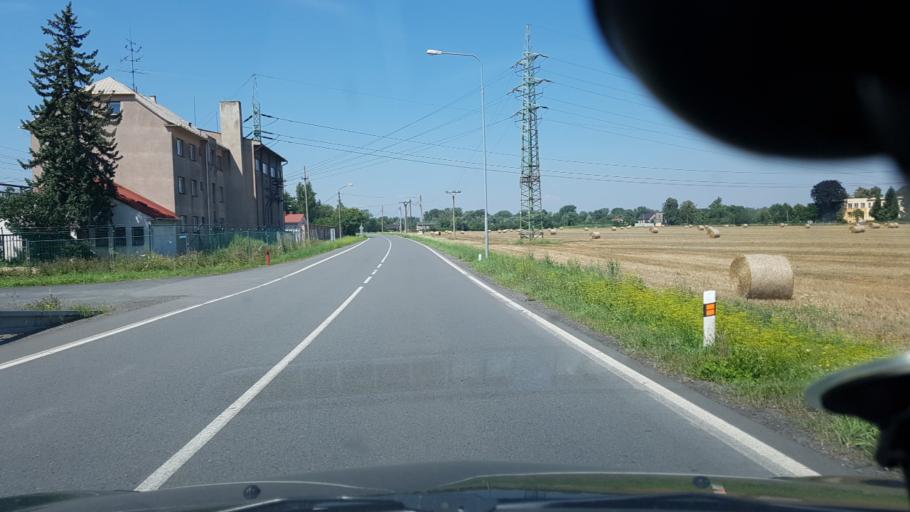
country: CZ
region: Moravskoslezsky
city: Bohumin
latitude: 49.8950
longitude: 18.3390
